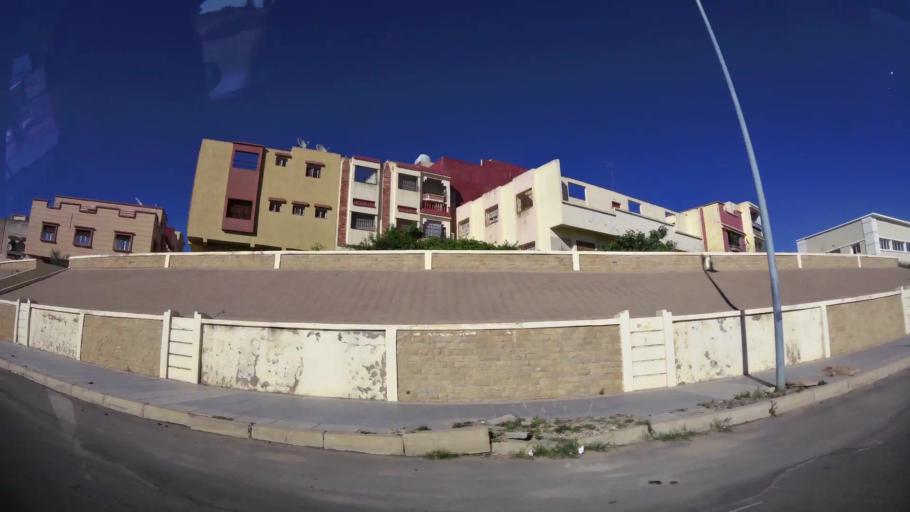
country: MA
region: Oriental
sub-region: Berkane-Taourirt
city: Ahfir
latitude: 34.9498
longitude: -2.1071
